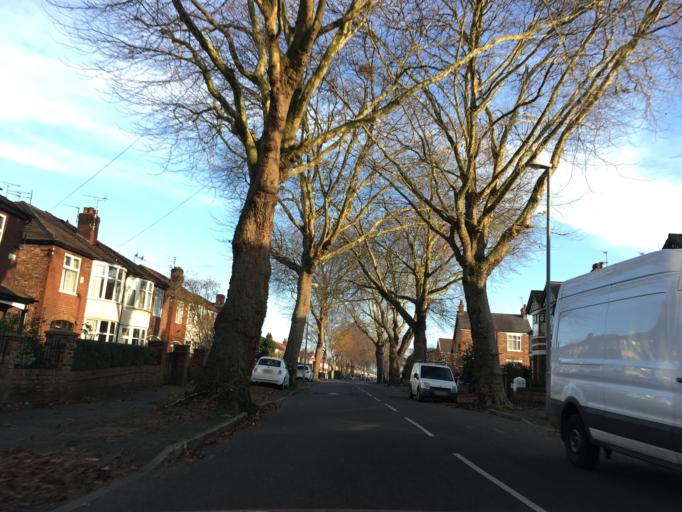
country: GB
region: England
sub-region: Manchester
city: Chorlton cum Hardy
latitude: 53.4457
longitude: -2.2727
